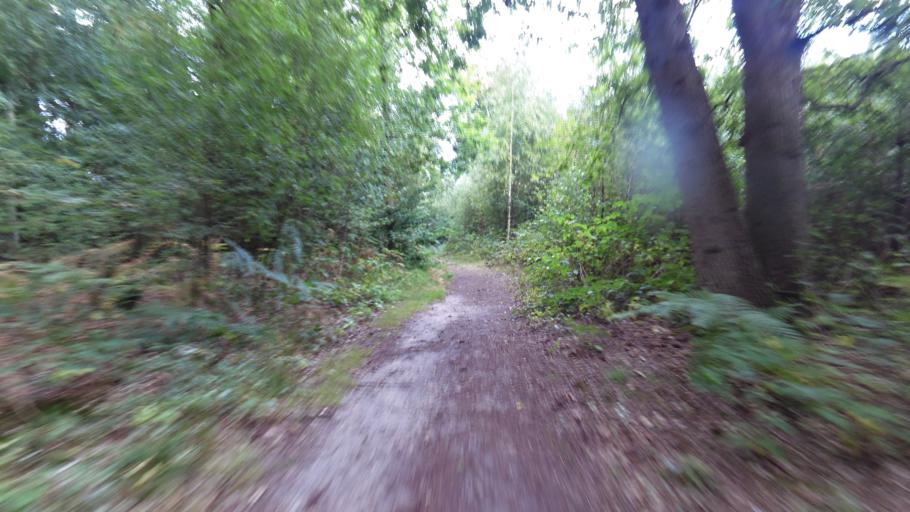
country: NL
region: Gelderland
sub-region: Gemeente Renkum
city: Renkum
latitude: 51.9853
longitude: 5.7259
